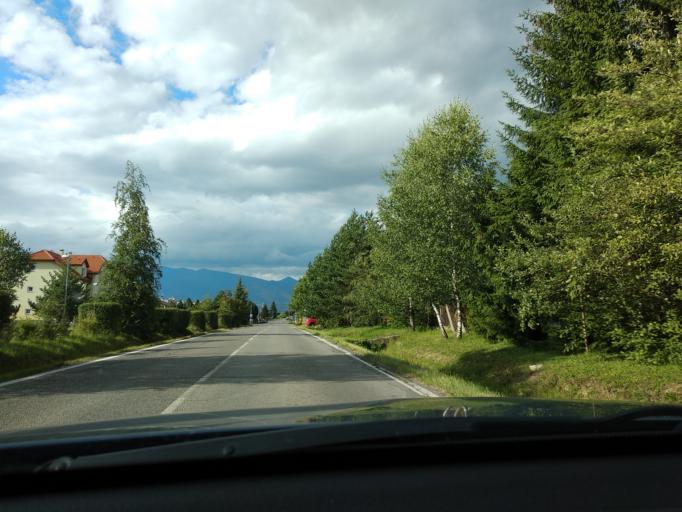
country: SK
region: Zilinsky
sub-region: Okres Zilina
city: Liptovsky Hradok
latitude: 49.0512
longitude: 19.7322
